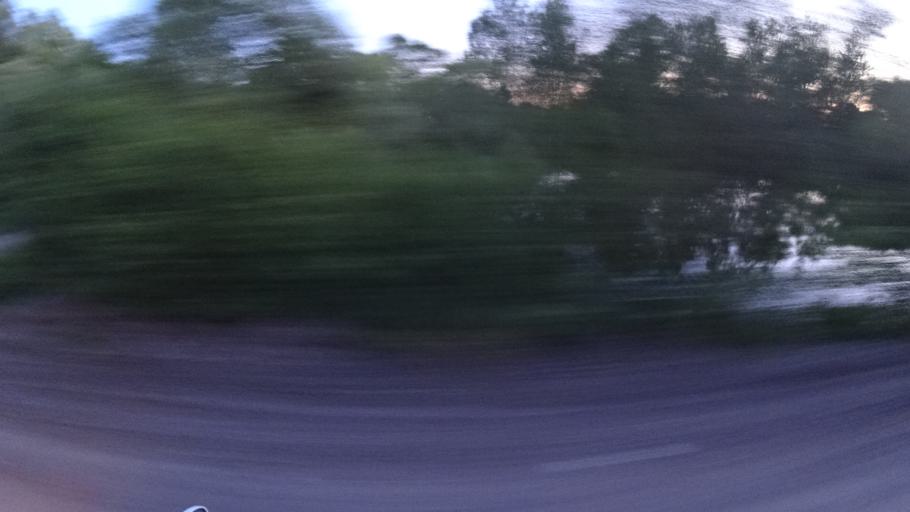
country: RU
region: Khabarovsk Krai
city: Khor
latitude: 47.8516
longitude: 134.9449
